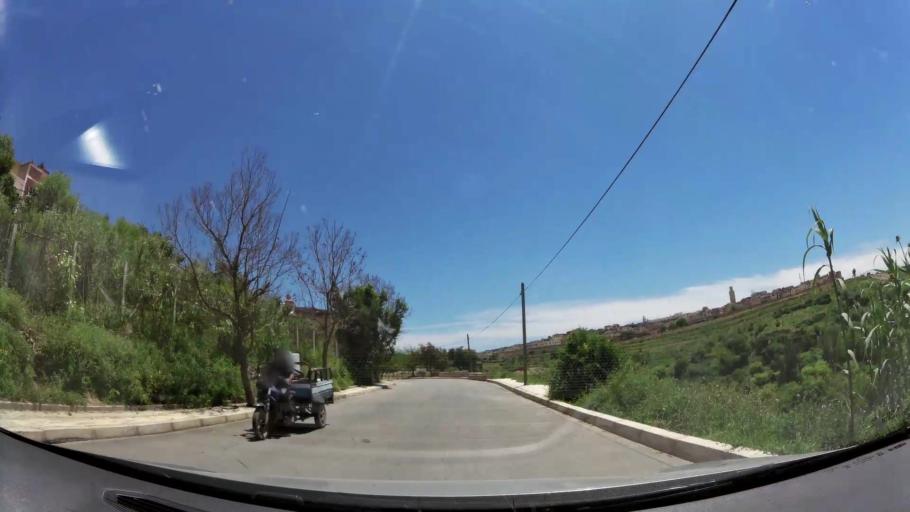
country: MA
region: Meknes-Tafilalet
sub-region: Meknes
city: Meknes
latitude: 33.9045
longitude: -5.5646
